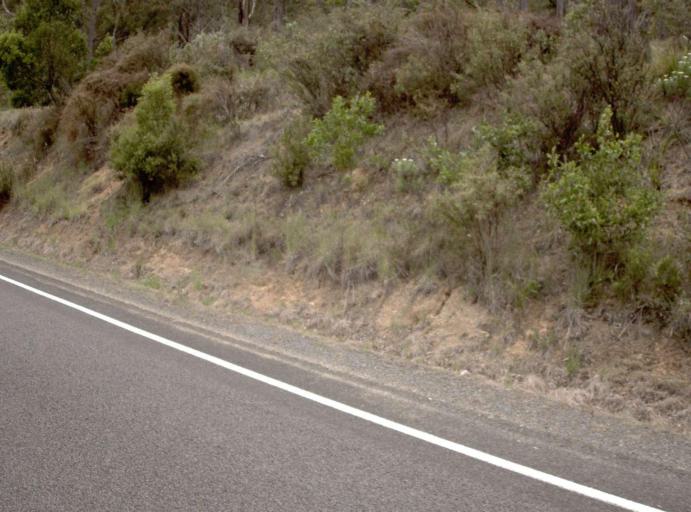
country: AU
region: New South Wales
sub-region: Bombala
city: Bombala
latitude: -37.2368
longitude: 149.2686
